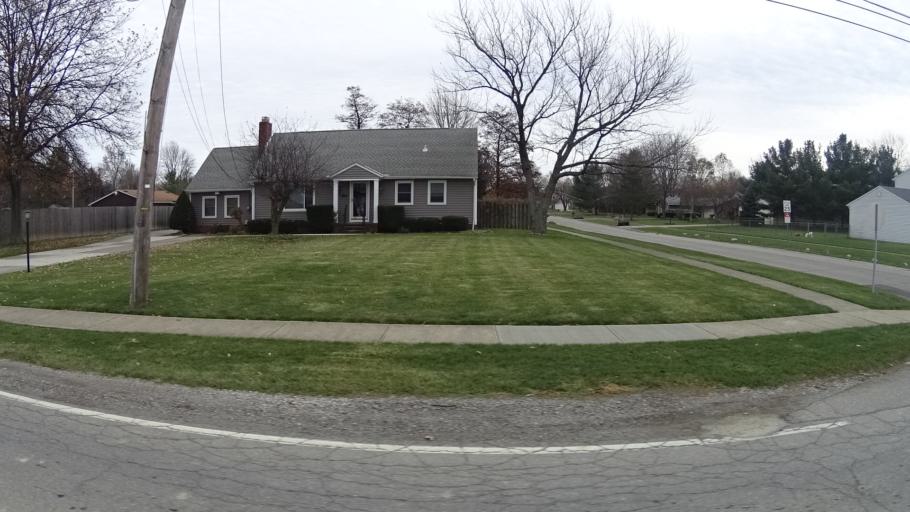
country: US
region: Ohio
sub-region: Cuyahoga County
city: Berea
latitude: 41.3468
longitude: -81.8770
